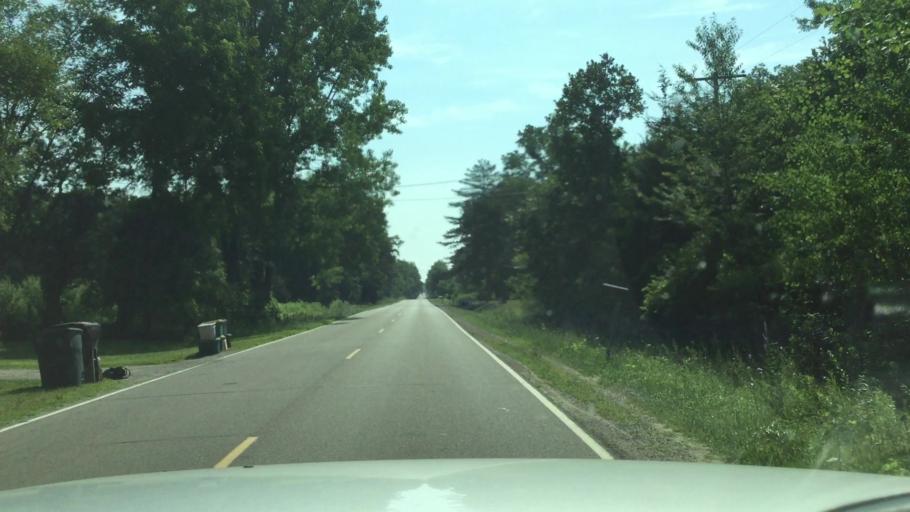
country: US
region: Michigan
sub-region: Genesee County
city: Montrose
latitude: 43.1334
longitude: -83.8404
